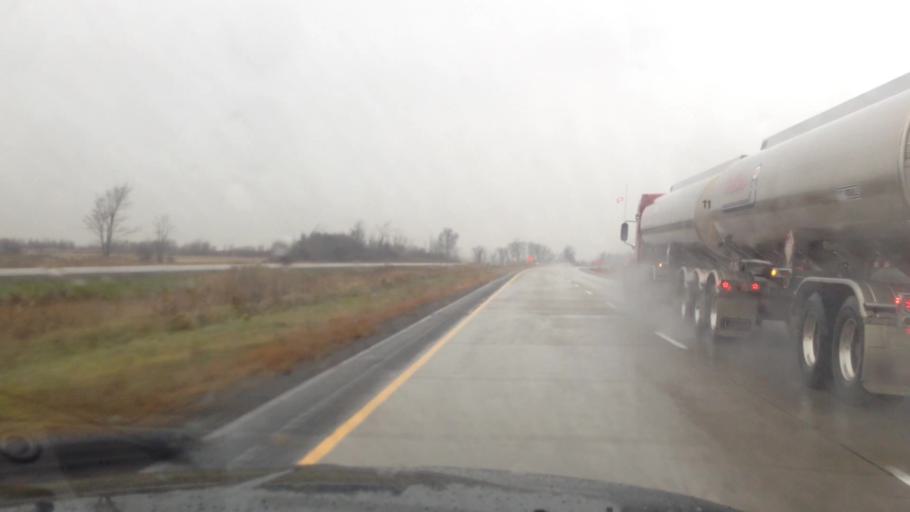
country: CA
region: Ontario
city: Hawkesbury
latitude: 45.4089
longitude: -74.7708
